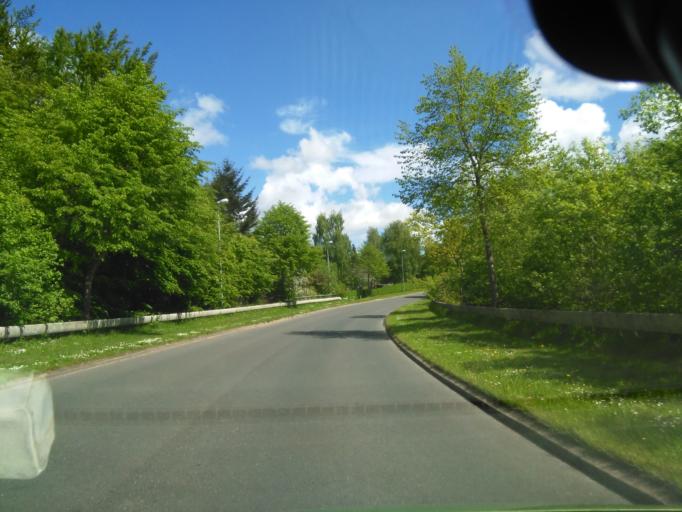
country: DK
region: Central Jutland
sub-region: Odder Kommune
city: Odder
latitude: 55.9848
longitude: 10.1348
